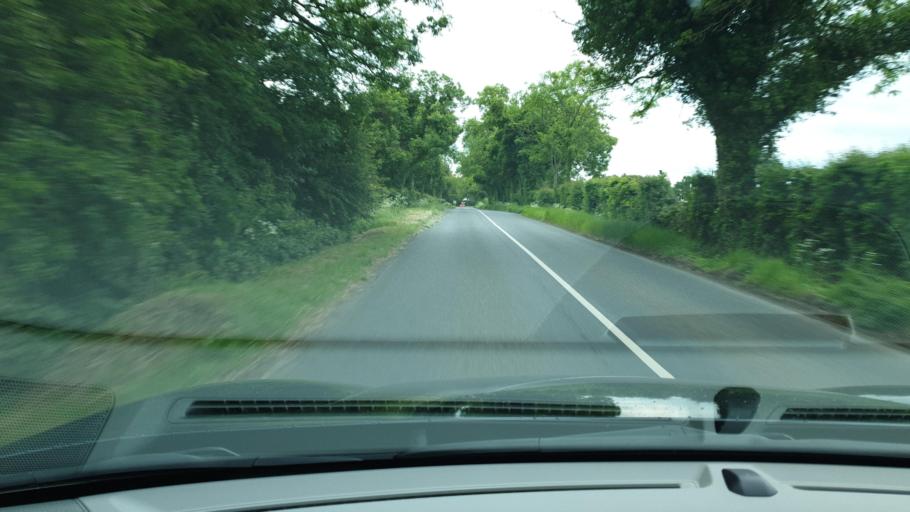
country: IE
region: Leinster
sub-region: An Mhi
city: Ashbourne
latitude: 53.5555
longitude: -6.3285
